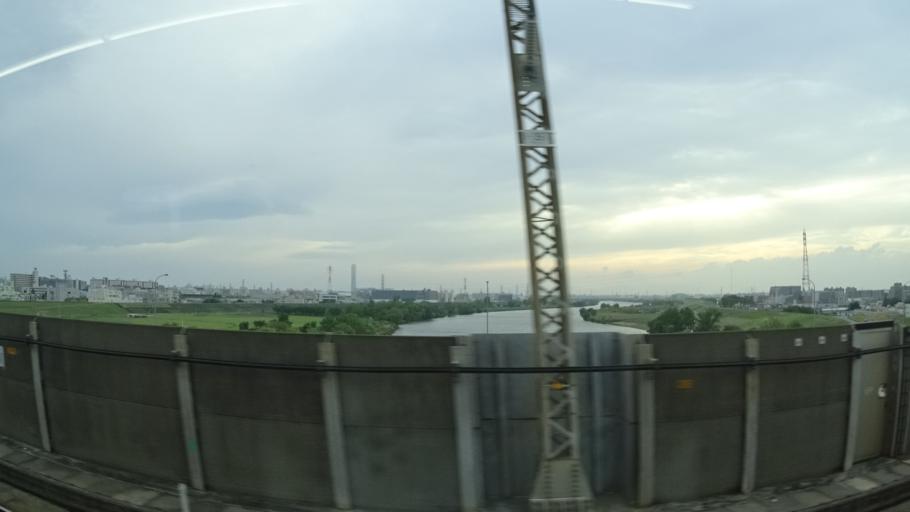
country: JP
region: Saitama
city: Shimotoda
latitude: 35.8001
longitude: 139.6851
